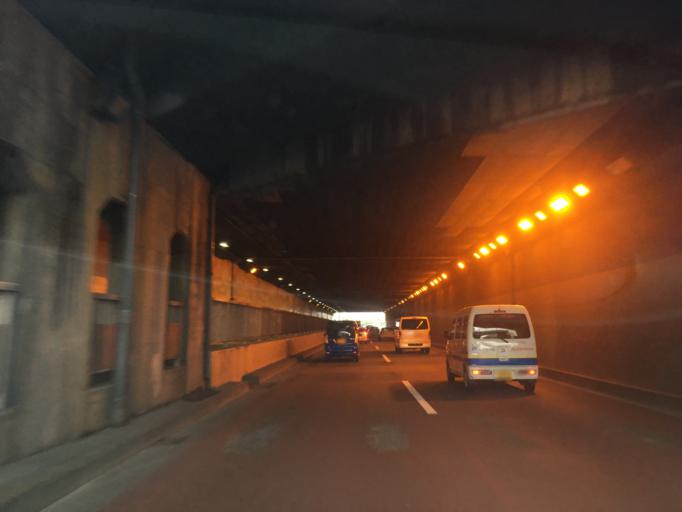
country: JP
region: Tokyo
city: Kokubunji
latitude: 35.6697
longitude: 139.4592
